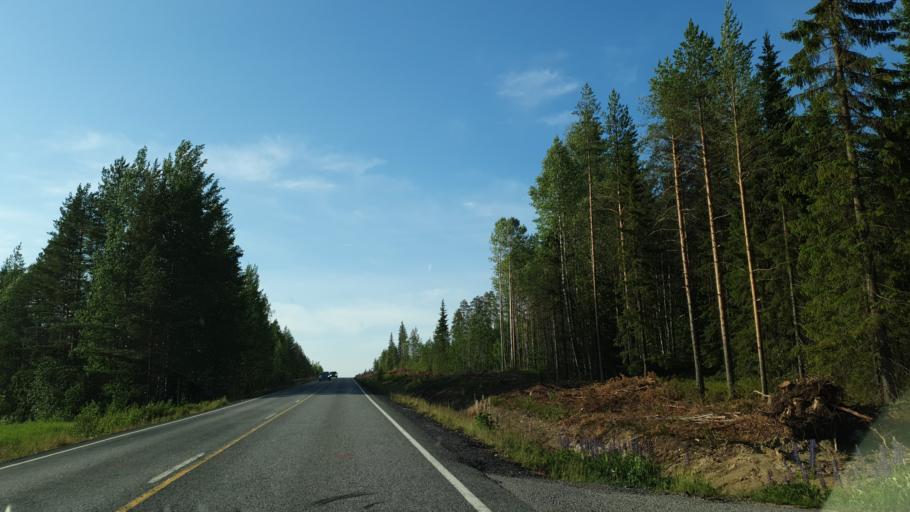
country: FI
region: Kainuu
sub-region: Kehys-Kainuu
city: Kuhmo
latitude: 64.0828
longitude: 29.4848
